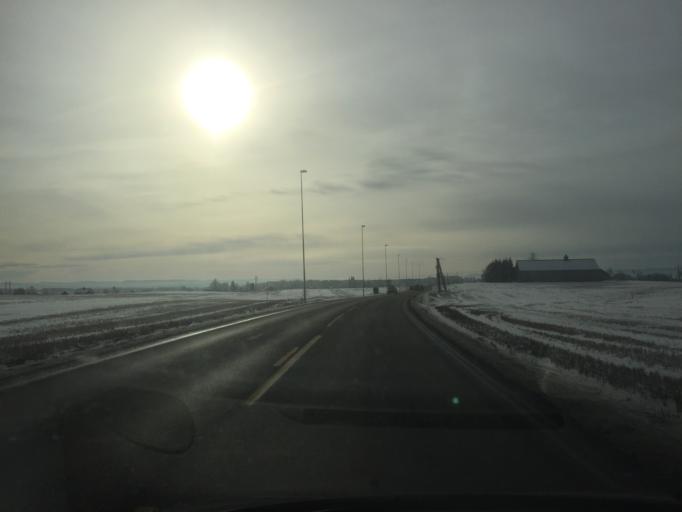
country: NO
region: Hedmark
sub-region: Loten
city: Loten
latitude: 60.8411
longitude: 11.3648
